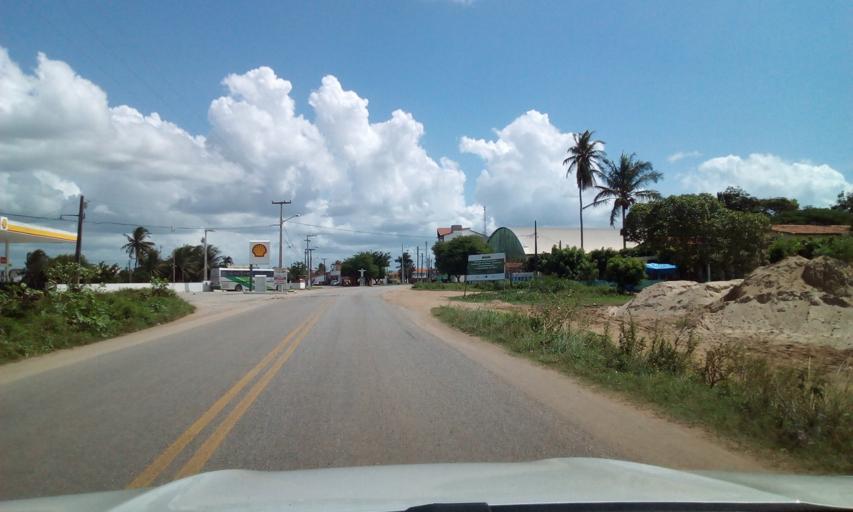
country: BR
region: Paraiba
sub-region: Guarabira
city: Guarabira
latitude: -6.8502
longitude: -35.3739
